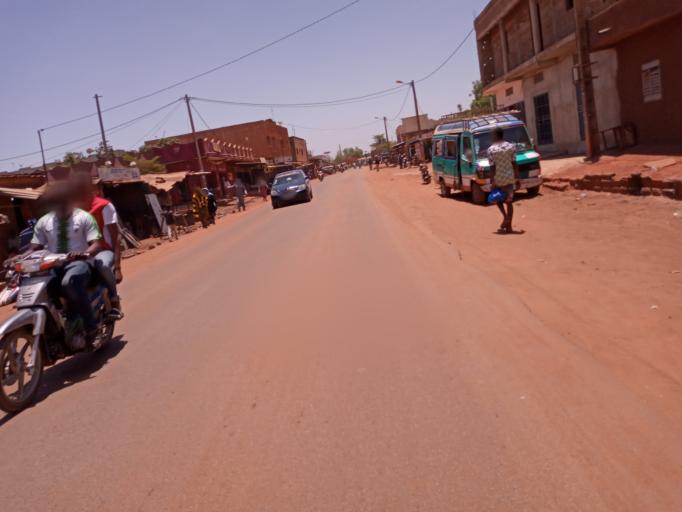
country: ML
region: Bamako
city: Bamako
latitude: 12.5752
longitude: -7.9702
